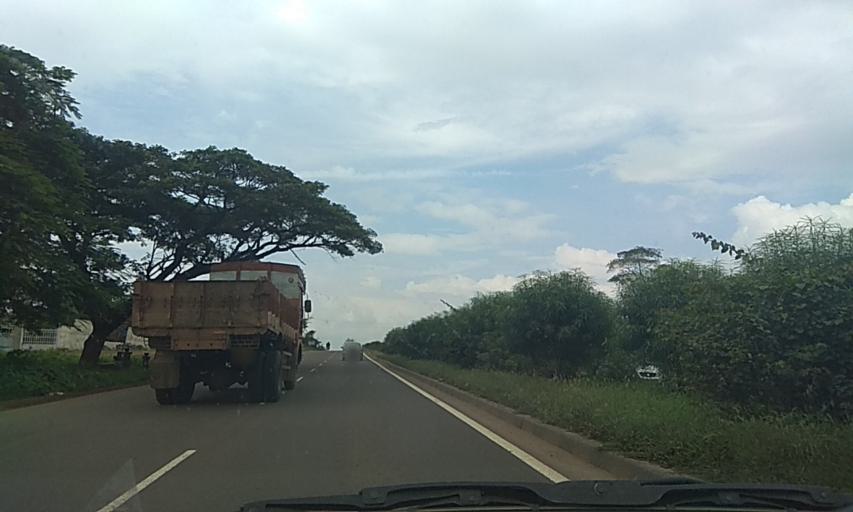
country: IN
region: Maharashtra
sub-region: Kolhapur
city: Kolhapur
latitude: 16.7844
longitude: 74.2783
